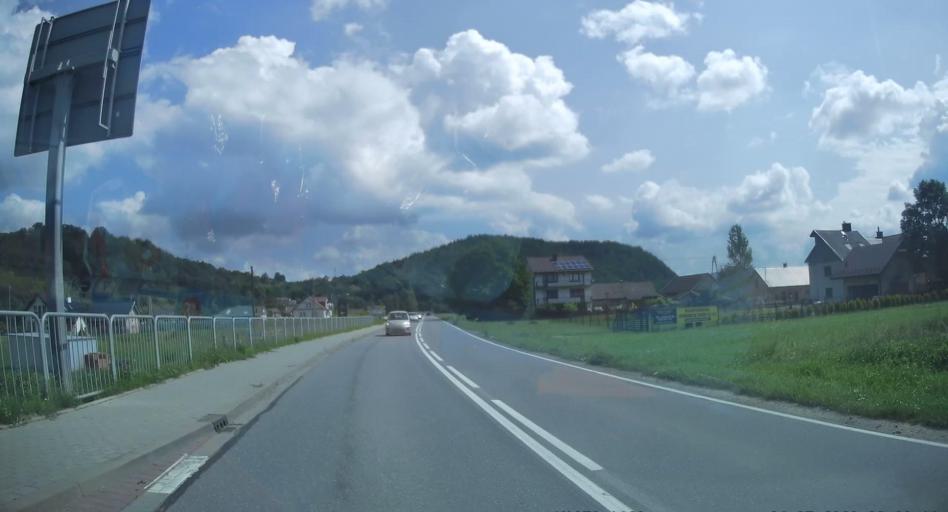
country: PL
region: Lesser Poland Voivodeship
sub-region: Powiat tarnowski
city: Zakliczyn
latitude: 49.8736
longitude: 20.8121
